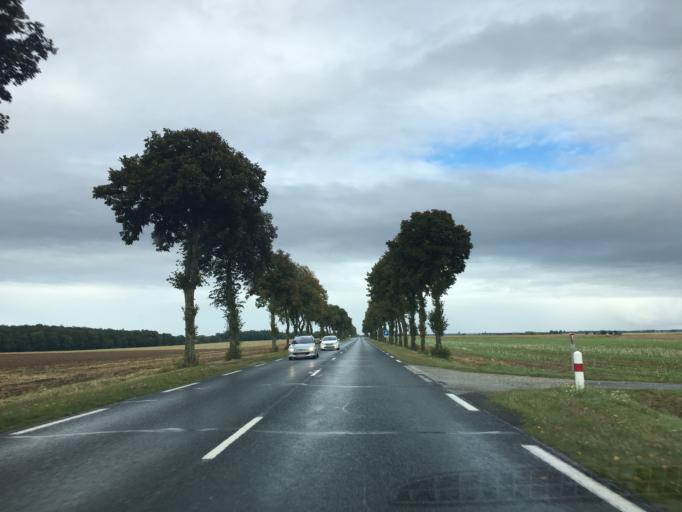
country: FR
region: Haute-Normandie
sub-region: Departement de l'Eure
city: Francheville
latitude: 48.7420
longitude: 0.8694
